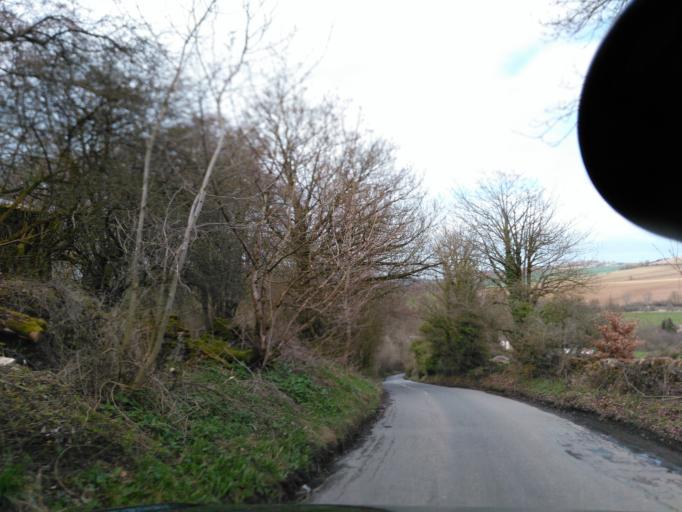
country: GB
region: England
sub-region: Gloucestershire
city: Charlton Kings
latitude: 51.8228
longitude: -2.0475
